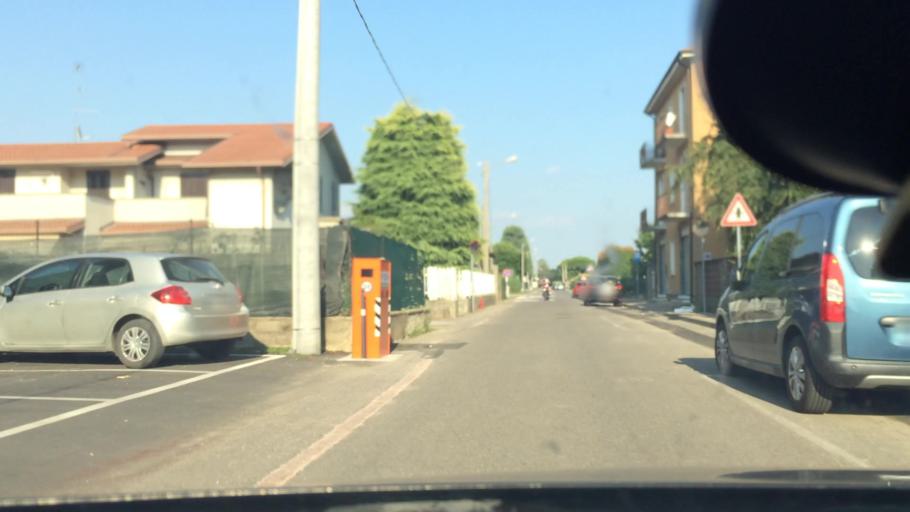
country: IT
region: Lombardy
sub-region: Provincia di Como
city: Turate
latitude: 45.6558
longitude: 9.0084
